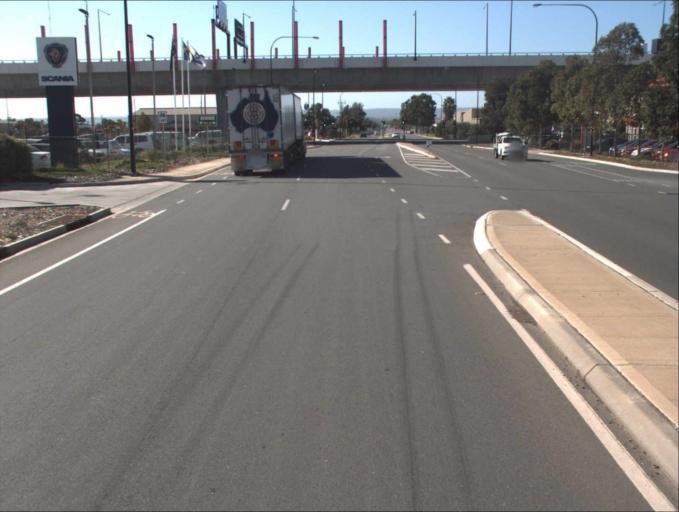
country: AU
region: South Australia
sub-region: Charles Sturt
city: Woodville North
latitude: -34.8406
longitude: 138.5620
